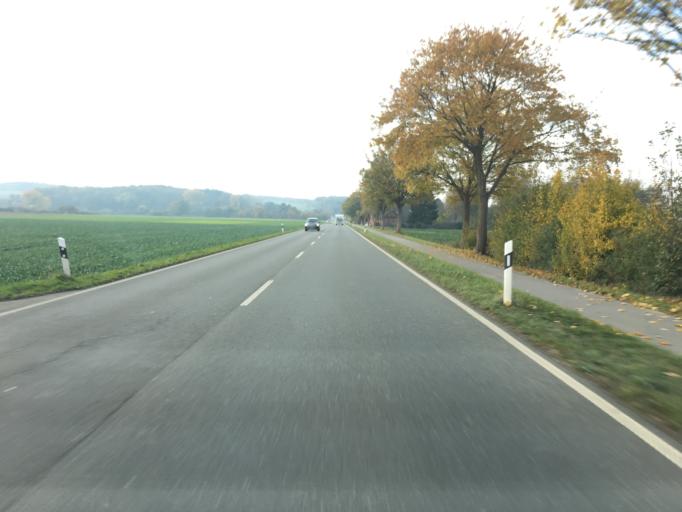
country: DE
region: North Rhine-Westphalia
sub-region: Regierungsbezirk Dusseldorf
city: Xanten
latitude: 51.6384
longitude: 6.4168
